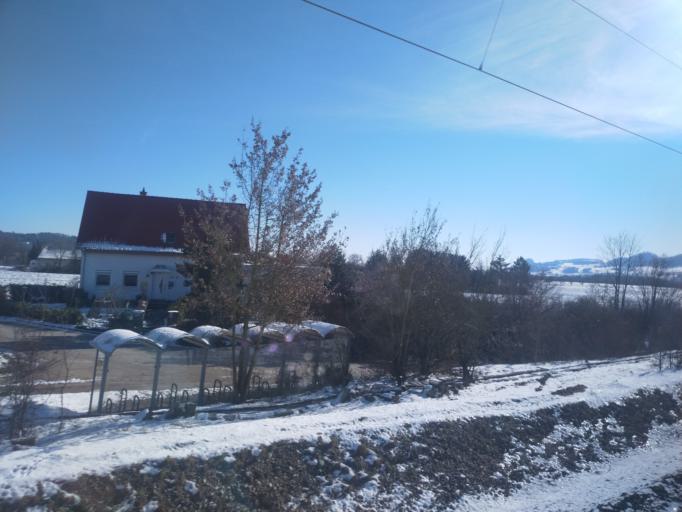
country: DE
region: Baden-Wuerttemberg
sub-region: Freiburg Region
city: Neuhausen
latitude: 47.8352
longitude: 8.7687
